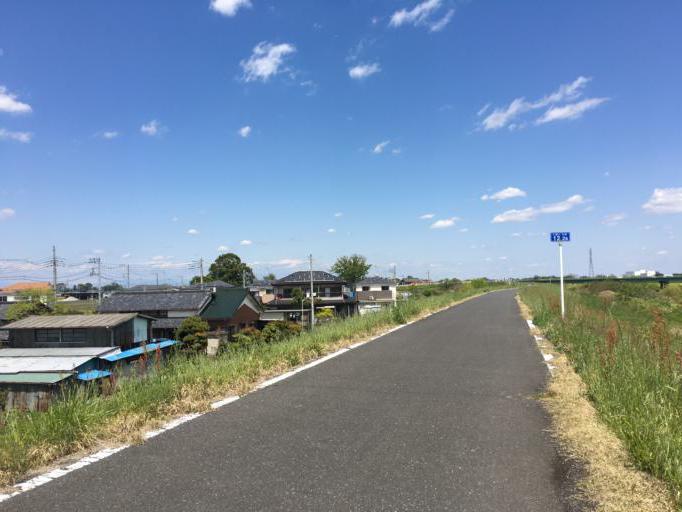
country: JP
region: Saitama
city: Kawagoe
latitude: 35.9388
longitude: 139.4639
